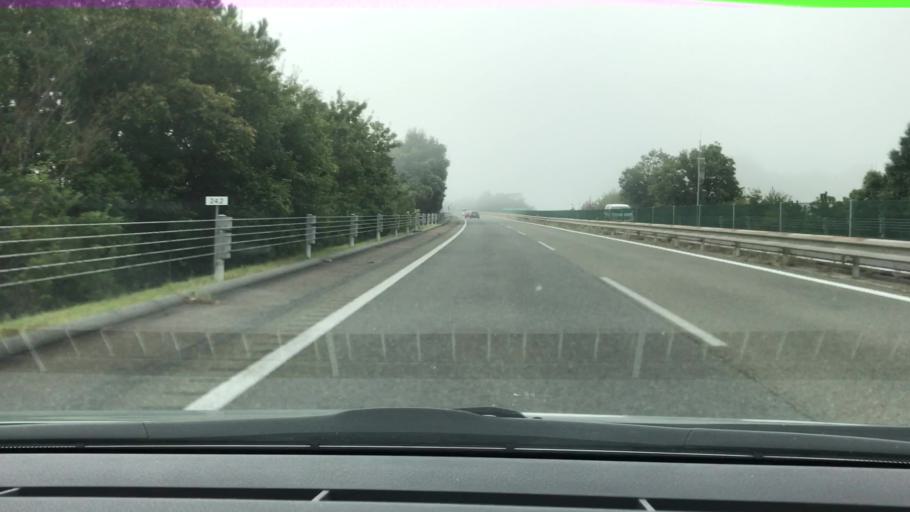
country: JP
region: Hyogo
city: Sasayama
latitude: 35.0795
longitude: 135.1688
